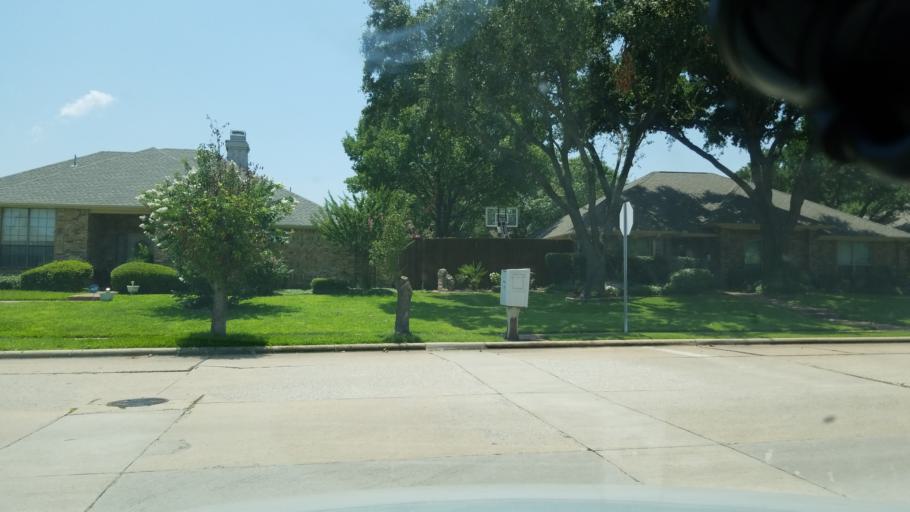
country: US
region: Texas
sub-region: Dallas County
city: Coppell
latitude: 32.9633
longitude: -96.9983
